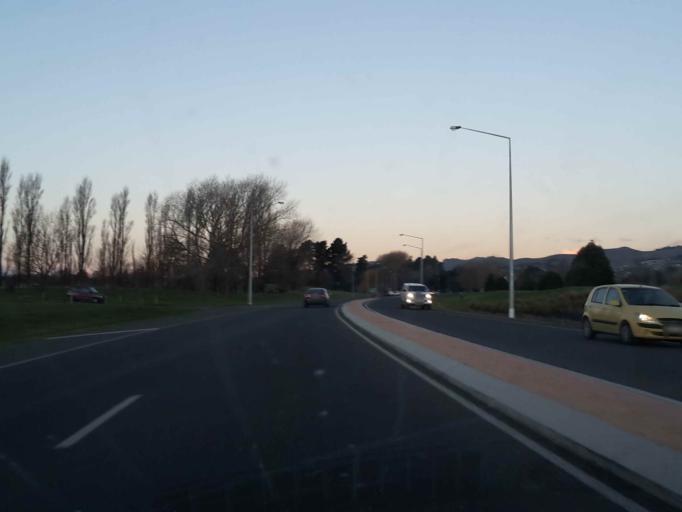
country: NZ
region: Canterbury
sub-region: Christchurch City
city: Christchurch
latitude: -43.5488
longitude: 172.5807
